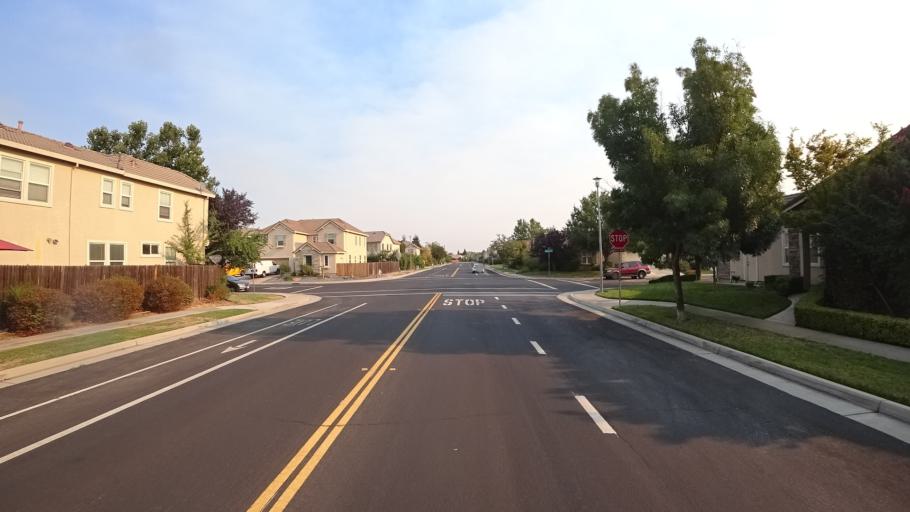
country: US
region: California
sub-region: Sacramento County
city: Laguna
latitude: 38.3818
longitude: -121.4384
